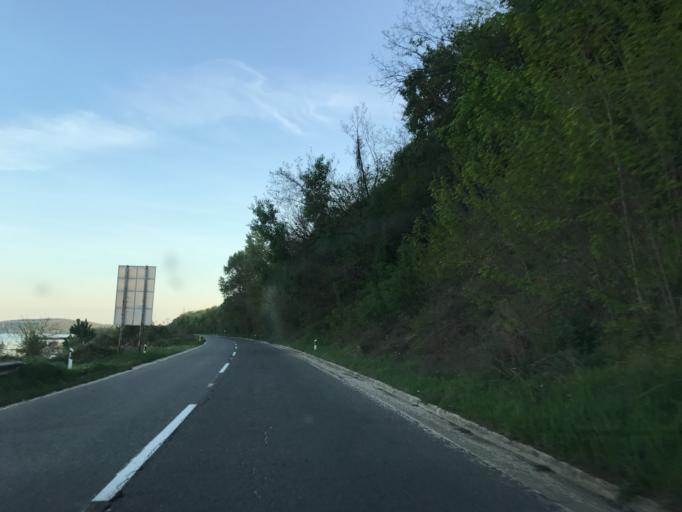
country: RO
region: Mehedinti
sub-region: Comuna Gogosu
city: Ostrovu Mare
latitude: 44.4720
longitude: 22.4493
